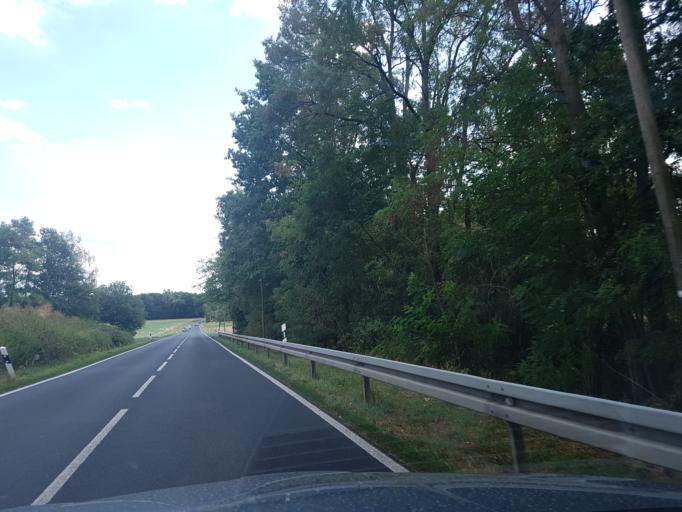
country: DE
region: Saxony
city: Priestewitz
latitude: 51.2597
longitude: 13.5467
